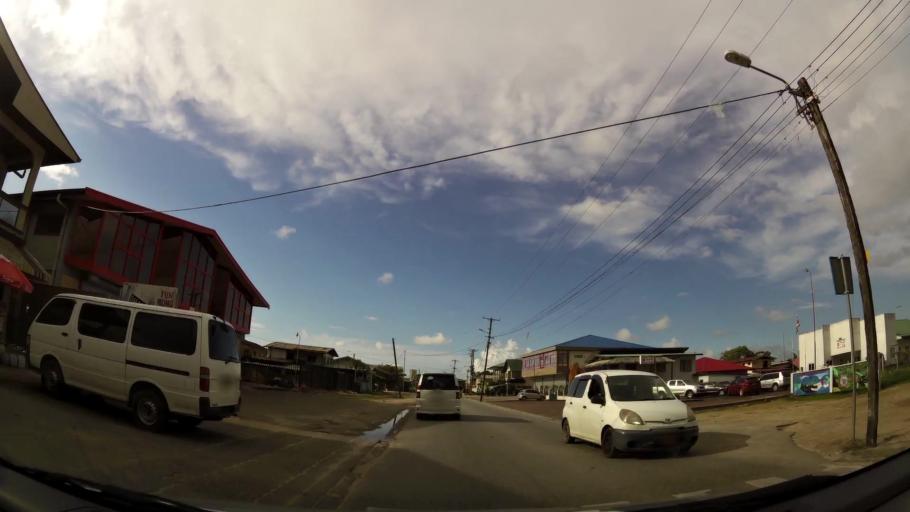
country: SR
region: Paramaribo
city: Paramaribo
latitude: 5.8432
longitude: -55.1814
